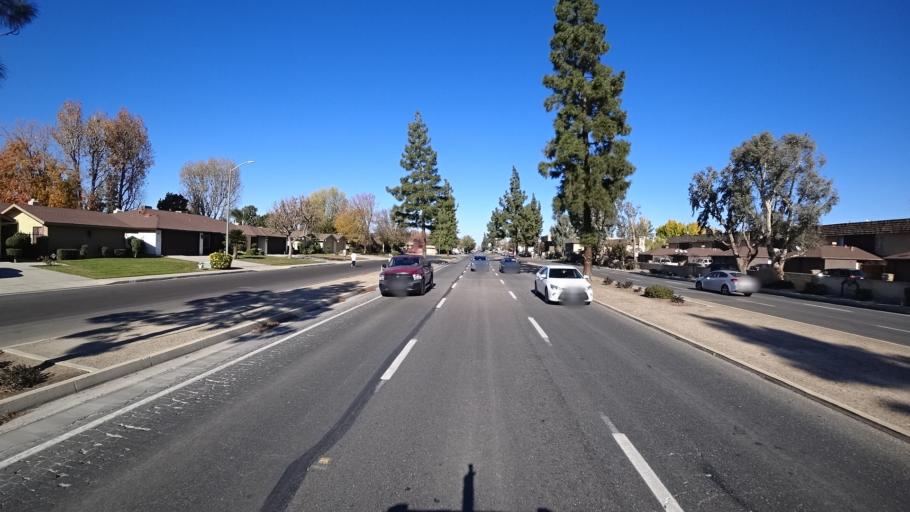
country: US
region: California
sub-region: Kern County
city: Bakersfield
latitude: 35.3506
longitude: -119.0613
